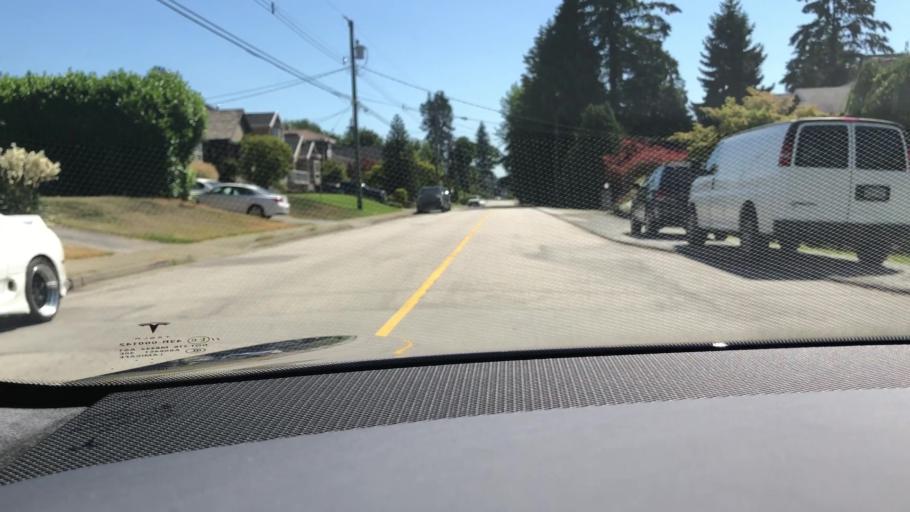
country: CA
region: British Columbia
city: Port Moody
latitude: 49.2454
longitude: -122.8713
